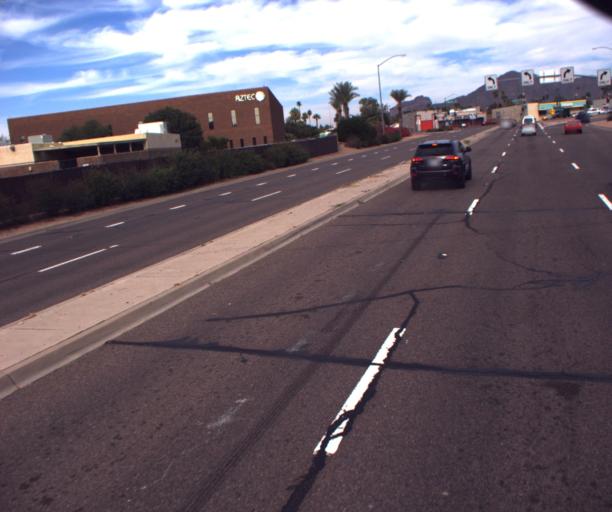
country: US
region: Arizona
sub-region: Maricopa County
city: Tempe Junction
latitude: 33.4642
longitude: -111.9822
